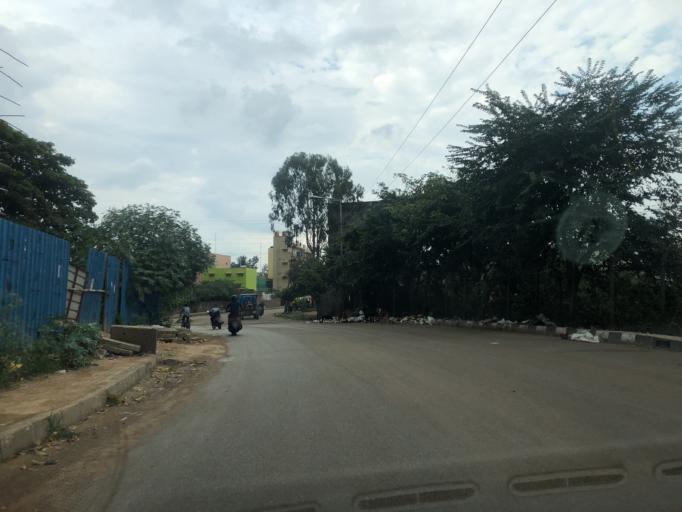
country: IN
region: Karnataka
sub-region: Bangalore Urban
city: Bangalore
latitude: 12.9872
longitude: 77.6973
